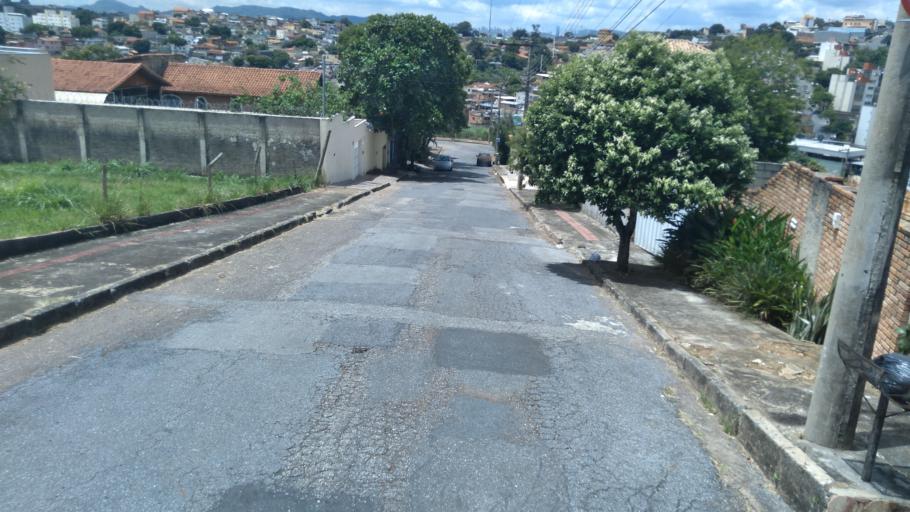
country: BR
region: Minas Gerais
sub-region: Contagem
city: Contagem
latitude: -19.9168
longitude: -44.0077
